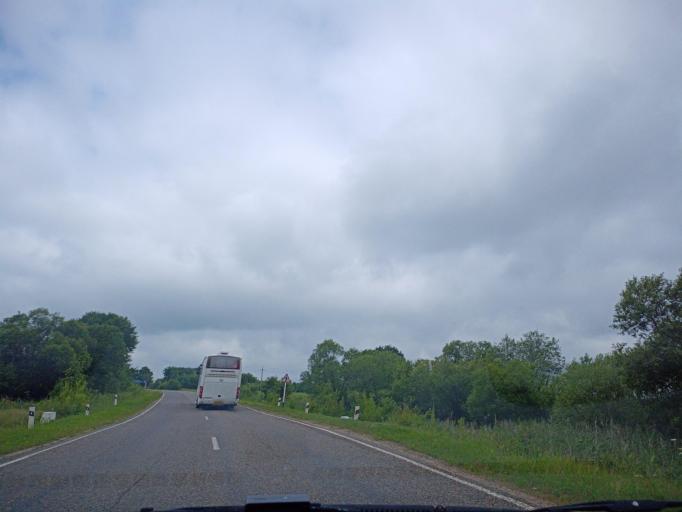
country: RU
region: Primorskiy
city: Novopokrovka
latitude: 45.9745
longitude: 134.2133
